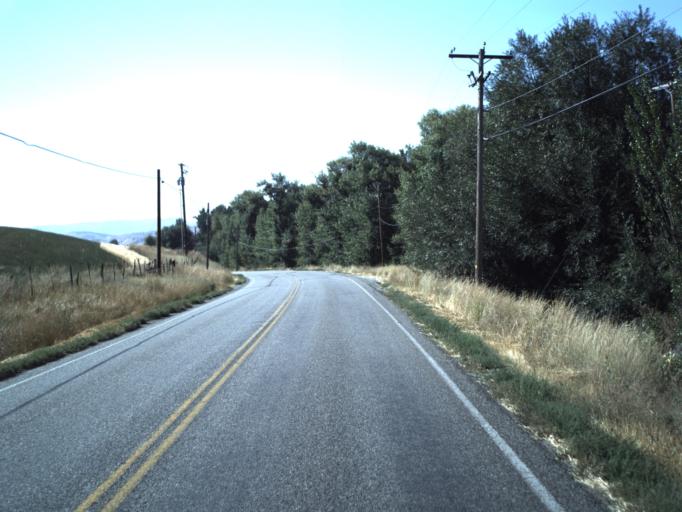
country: US
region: Utah
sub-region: Cache County
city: Hyrum
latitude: 41.5952
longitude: -111.8361
